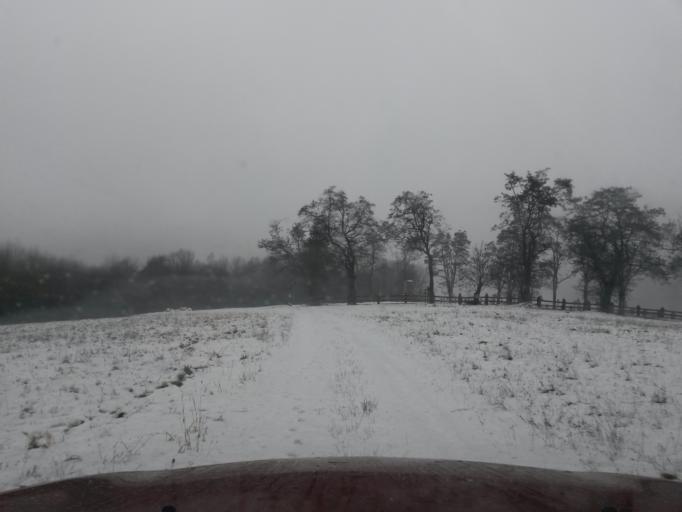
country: SK
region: Presovsky
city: Stropkov
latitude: 49.2368
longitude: 21.7532
